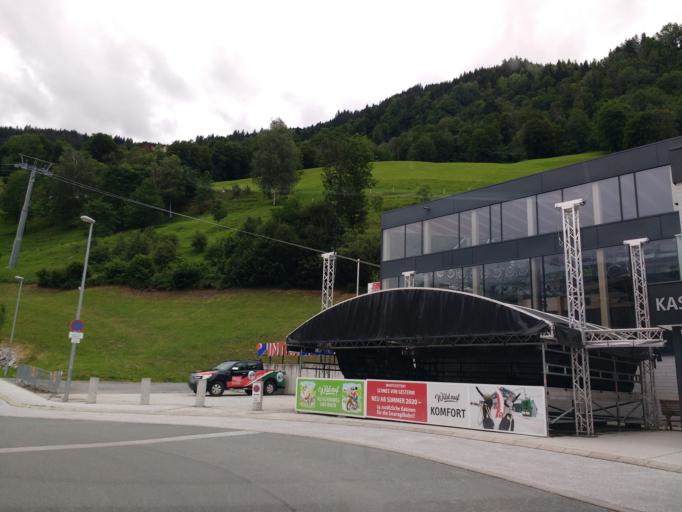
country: AT
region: Salzburg
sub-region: Politischer Bezirk Zell am See
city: Bramberg am Wildkogel
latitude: 47.2723
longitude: 12.3406
